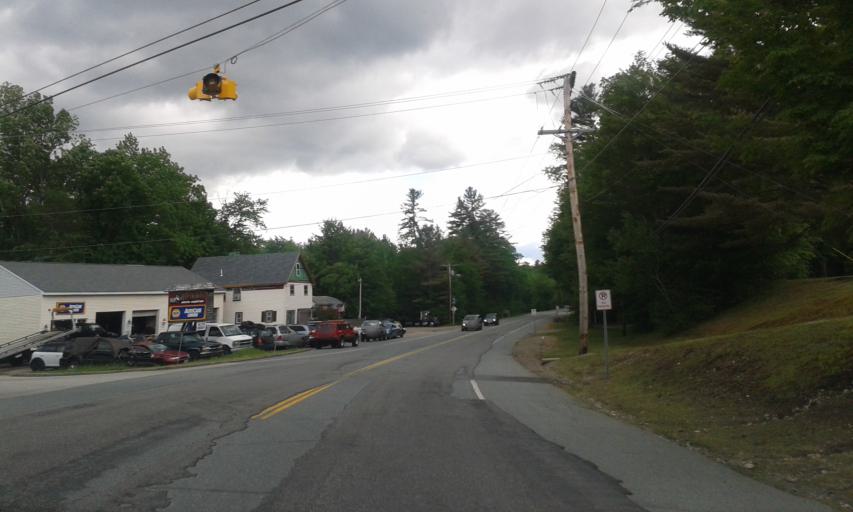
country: US
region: New Hampshire
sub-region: Grafton County
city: Woodstock
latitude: 44.0476
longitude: -71.6864
